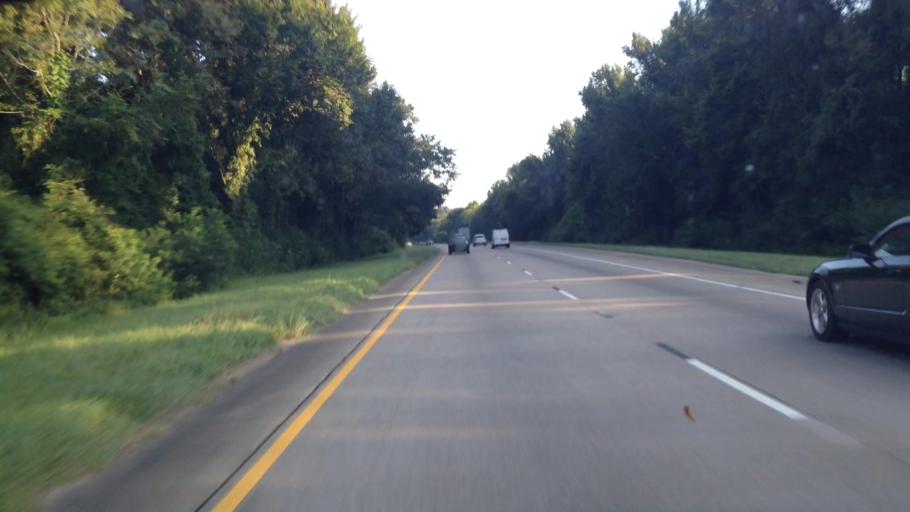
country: US
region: Louisiana
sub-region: Ascension Parish
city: Prairieville
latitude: 30.3009
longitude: -90.9923
